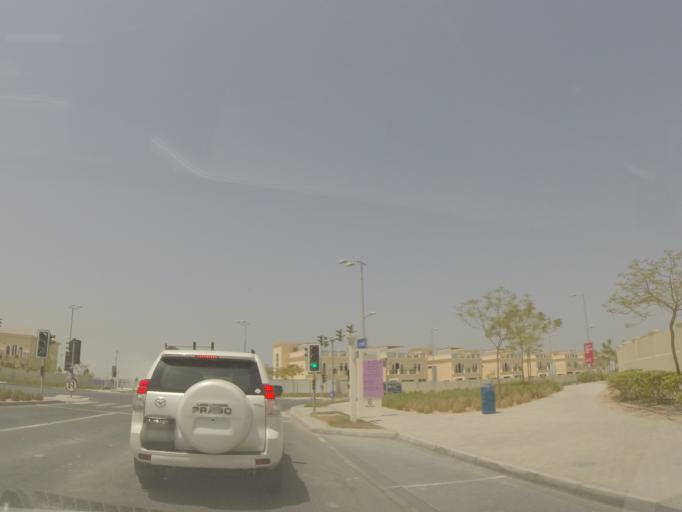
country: AE
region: Dubai
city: Dubai
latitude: 25.0468
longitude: 55.1679
